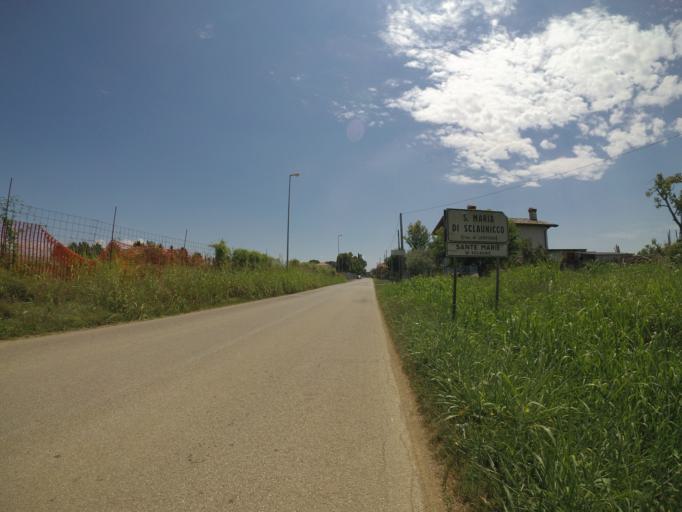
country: IT
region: Friuli Venezia Giulia
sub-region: Provincia di Udine
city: Lestizza
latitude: 45.9743
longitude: 13.1567
